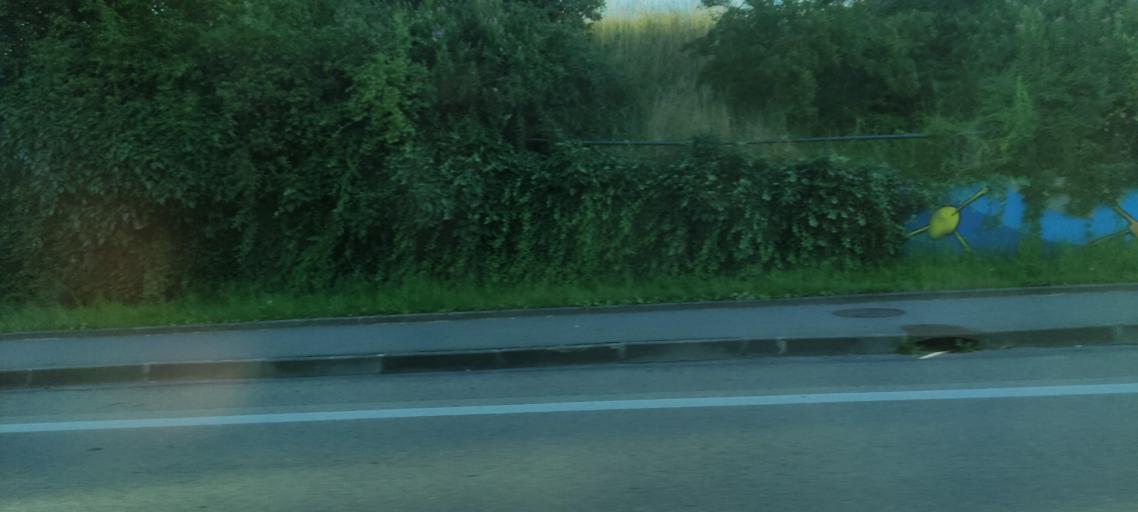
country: CZ
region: Jihocesky
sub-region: Okres Jindrichuv Hradec
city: Jindrichuv Hradec
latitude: 49.1492
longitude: 15.0198
